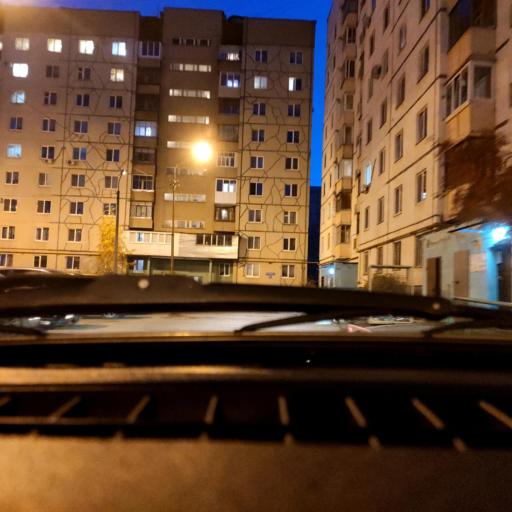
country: RU
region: Bashkortostan
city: Ufa
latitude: 54.7830
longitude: 56.1093
